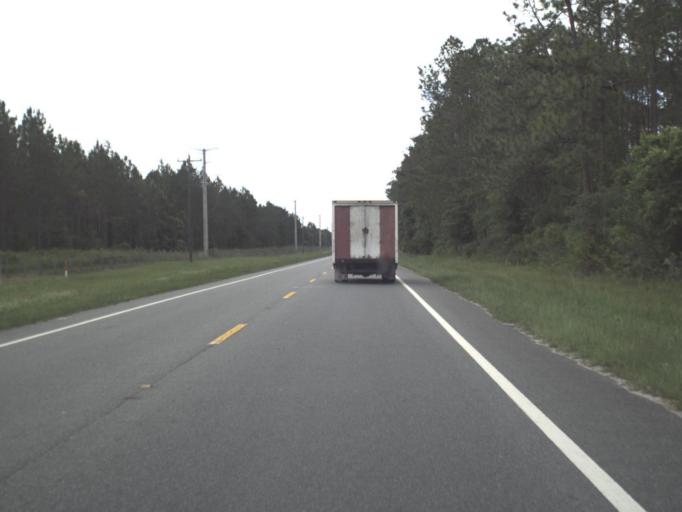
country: US
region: Florida
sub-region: Clay County
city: Asbury Lake
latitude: 29.9296
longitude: -81.8974
